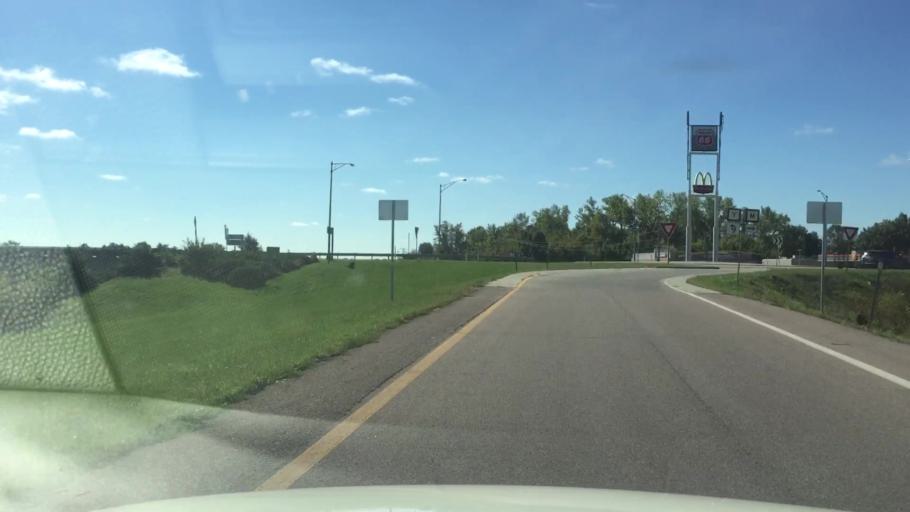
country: US
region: Missouri
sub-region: Boone County
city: Ashland
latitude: 38.7752
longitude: -92.2524
